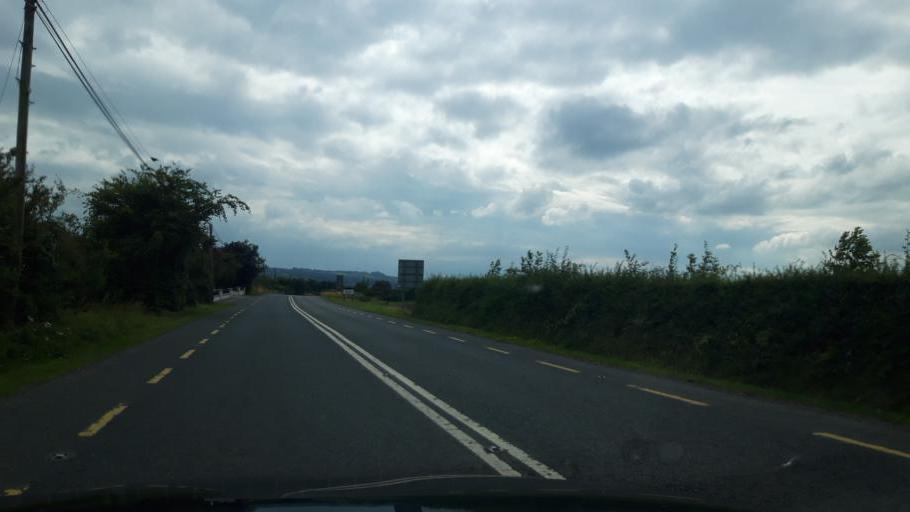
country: IE
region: Leinster
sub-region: Kilkenny
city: Castlecomer
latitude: 52.8595
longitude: -7.1128
